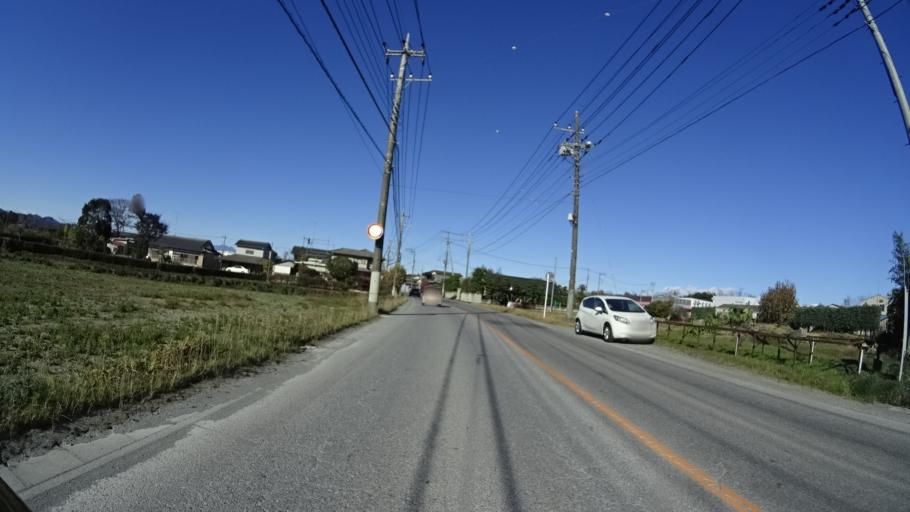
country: JP
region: Tochigi
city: Mibu
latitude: 36.4492
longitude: 139.7564
